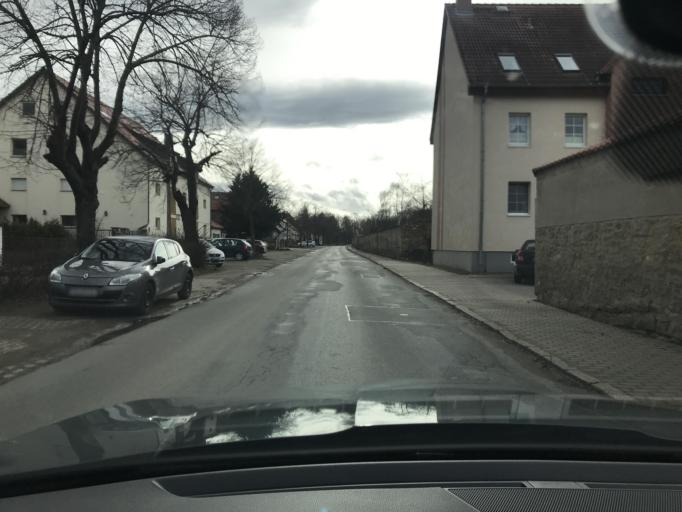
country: DE
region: Saxony-Anhalt
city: Wegeleben
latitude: 51.8842
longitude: 11.1764
